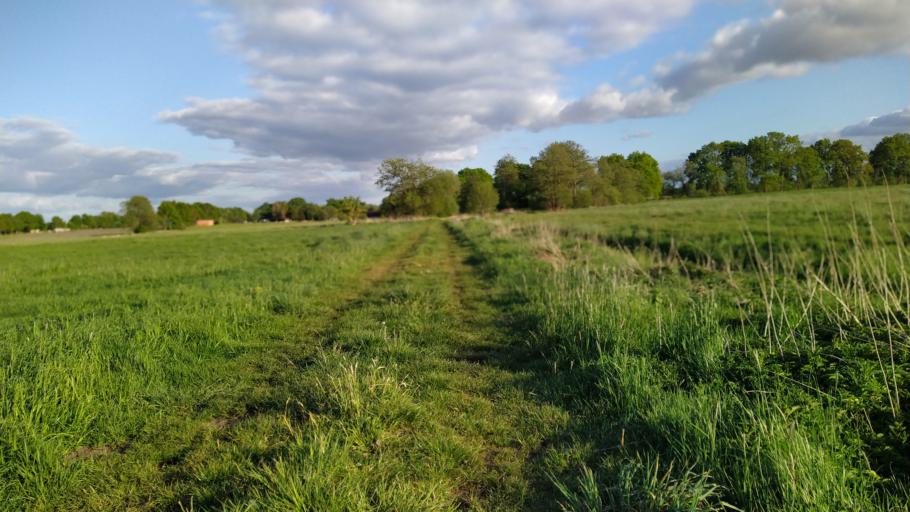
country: DE
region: Lower Saxony
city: Farven
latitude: 53.4464
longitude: 9.3374
